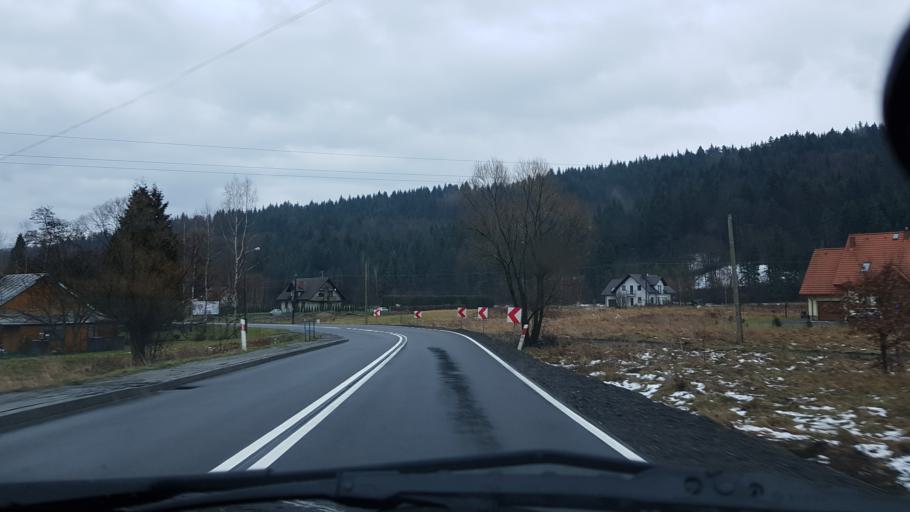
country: PL
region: Lesser Poland Voivodeship
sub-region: Powiat suski
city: Kukow
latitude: 49.7299
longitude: 19.4905
